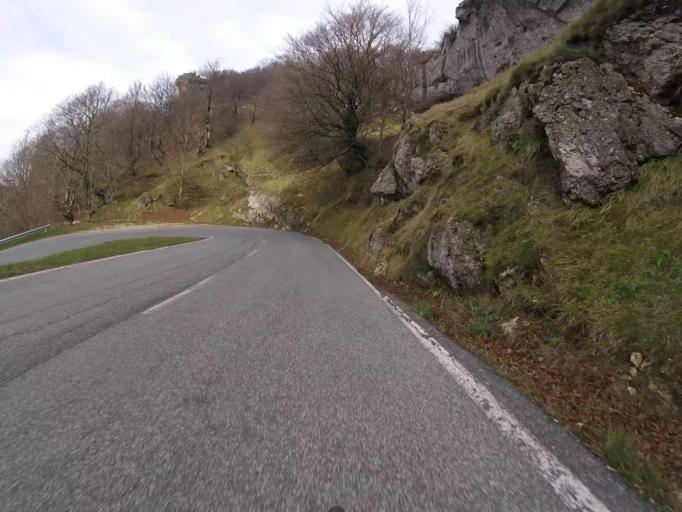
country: ES
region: Navarre
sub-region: Provincia de Navarra
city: Olazagutia
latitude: 42.8600
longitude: -2.1818
